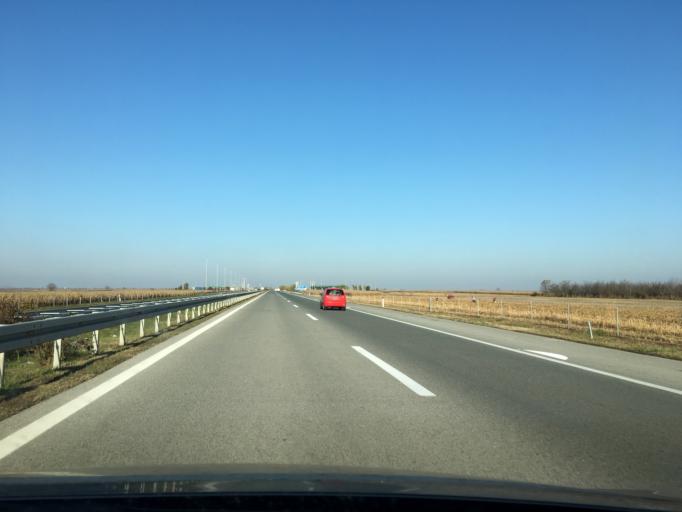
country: RS
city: Rumenka
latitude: 45.3238
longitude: 19.7863
